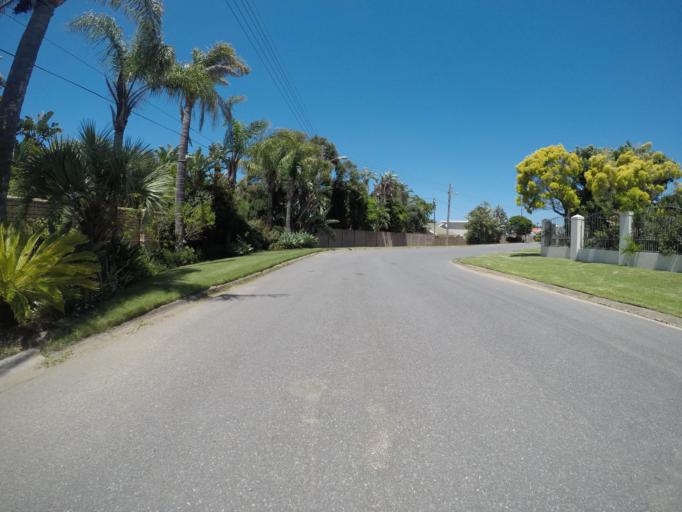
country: ZA
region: Eastern Cape
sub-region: Buffalo City Metropolitan Municipality
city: East London
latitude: -32.9663
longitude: 27.9548
